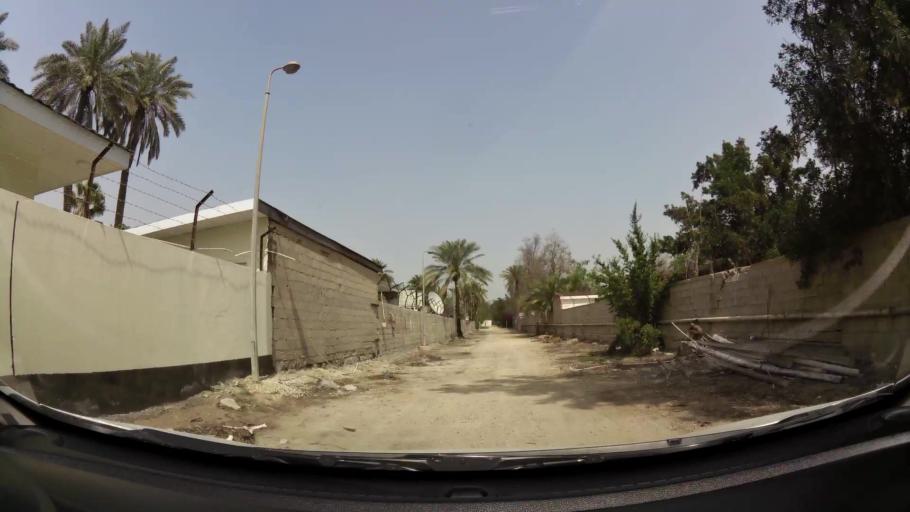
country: BH
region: Manama
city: Jidd Hafs
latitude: 26.2237
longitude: 50.5030
